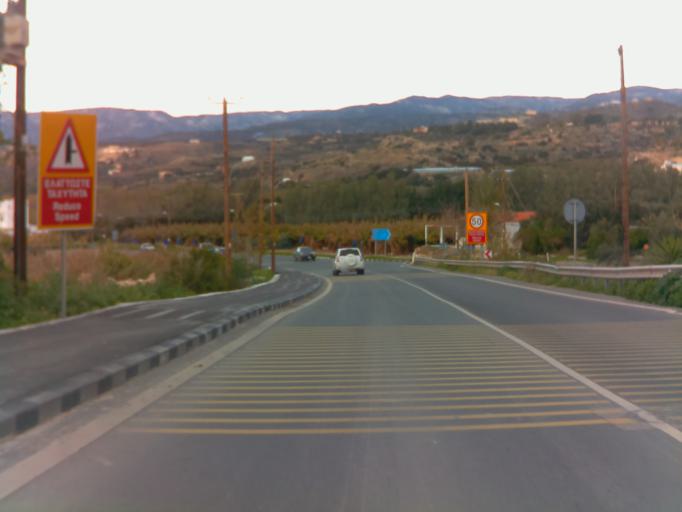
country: CY
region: Pafos
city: Kissonerga
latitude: 34.8312
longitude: 32.3927
